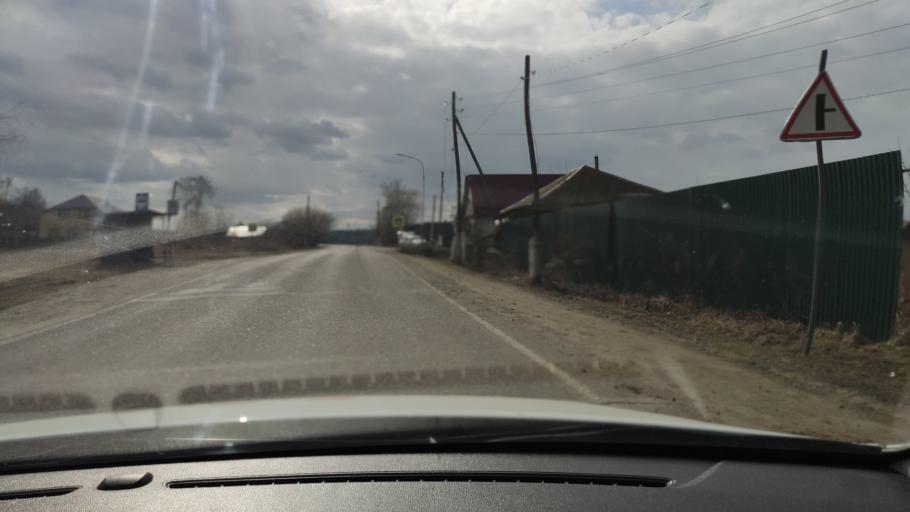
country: RU
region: Tatarstan
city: Vysokaya Gora
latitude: 56.1924
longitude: 49.2062
